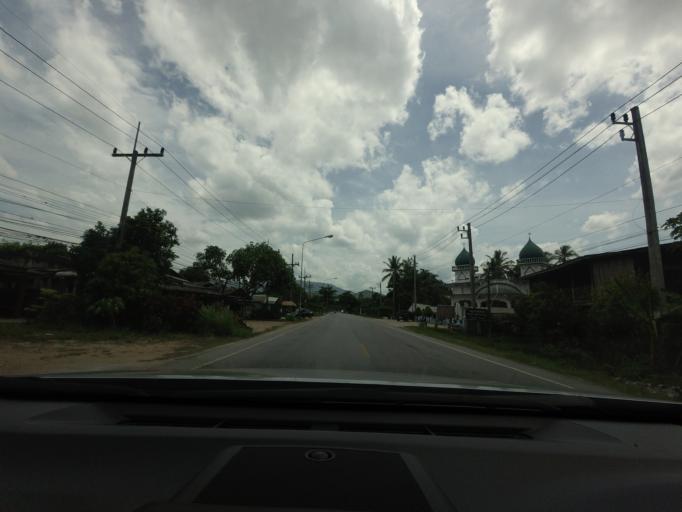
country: TH
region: Yala
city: Raman
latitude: 6.4597
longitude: 101.3668
